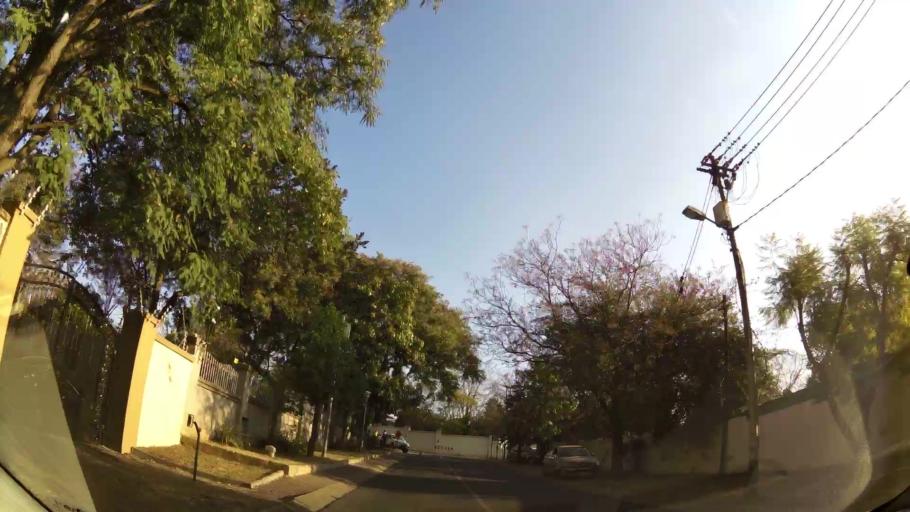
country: ZA
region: Gauteng
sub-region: City of Johannesburg Metropolitan Municipality
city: Diepsloot
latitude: -26.0558
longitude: 27.9959
